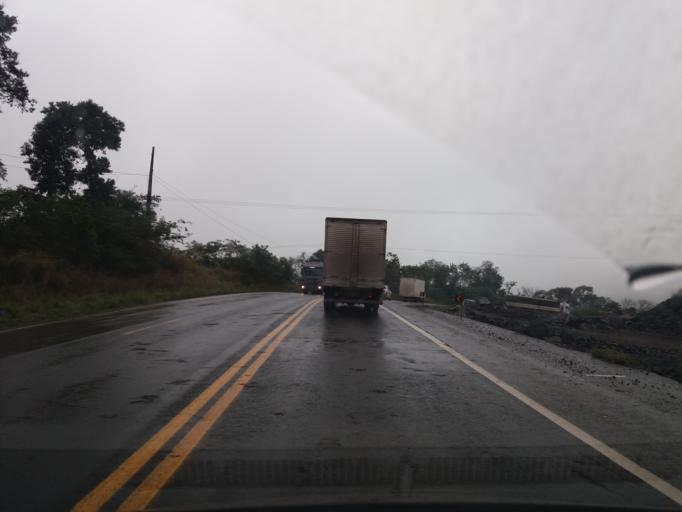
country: BR
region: Parana
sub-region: Realeza
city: Realeza
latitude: -25.4727
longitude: -53.5873
